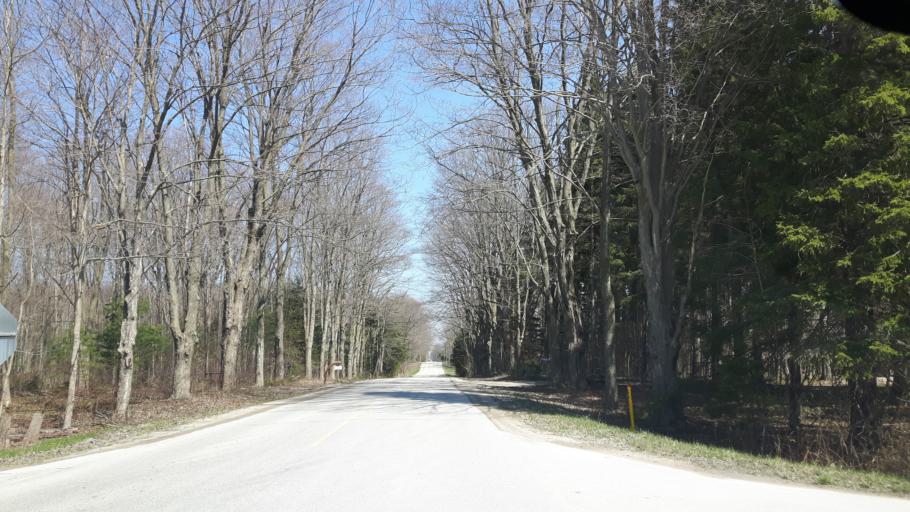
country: CA
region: Ontario
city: Goderich
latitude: 43.6058
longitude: -81.6847
